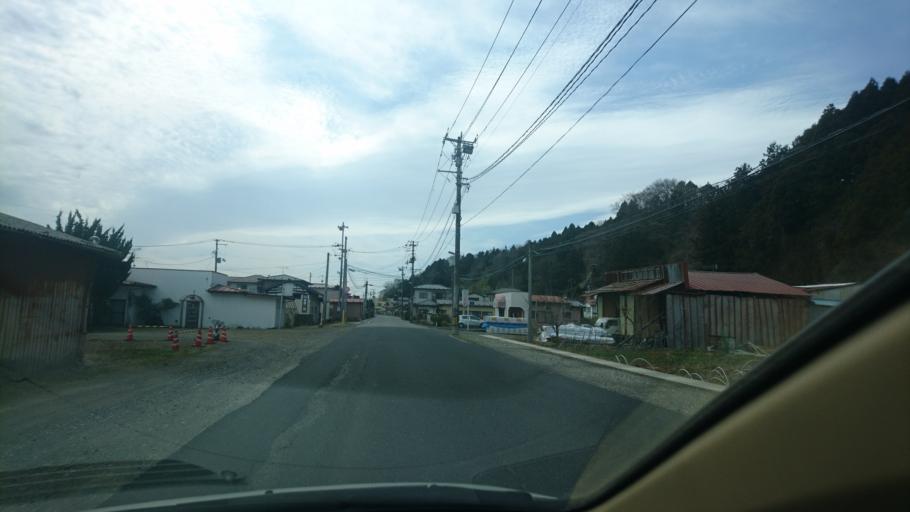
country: JP
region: Miyagi
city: Furukawa
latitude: 38.7538
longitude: 141.0208
